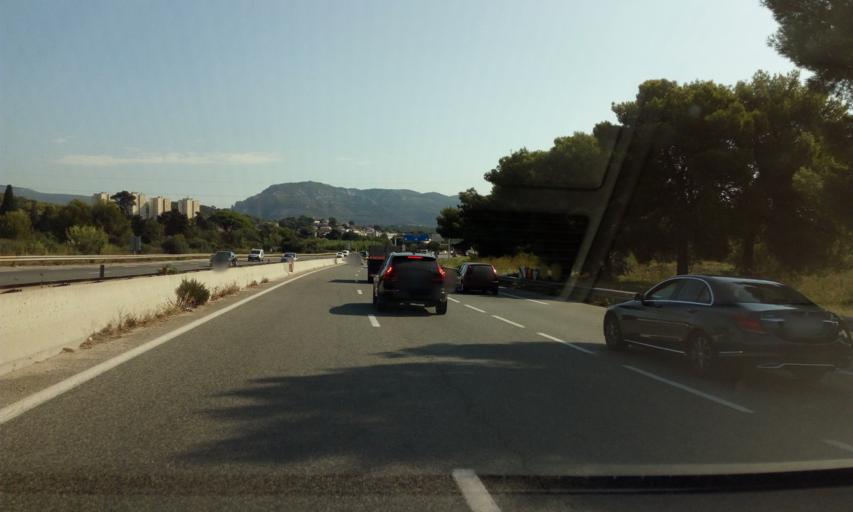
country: FR
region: Provence-Alpes-Cote d'Azur
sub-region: Departement du Var
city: Ollioules
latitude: 43.1243
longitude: 5.8723
